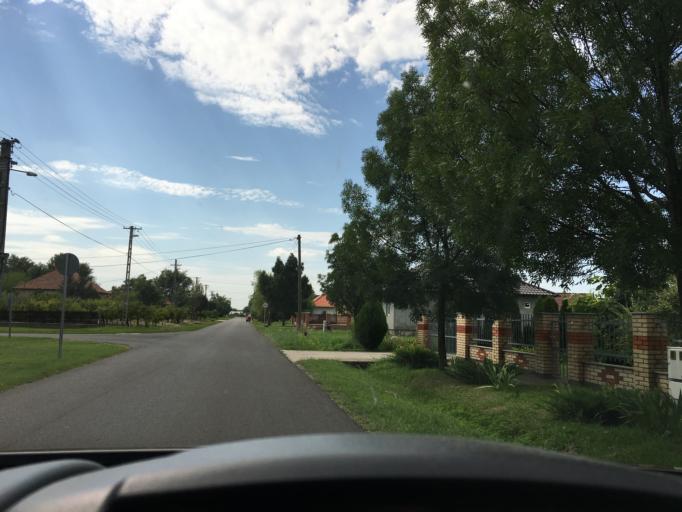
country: HU
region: Csongrad
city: Morahalom
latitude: 46.2115
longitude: 19.8740
